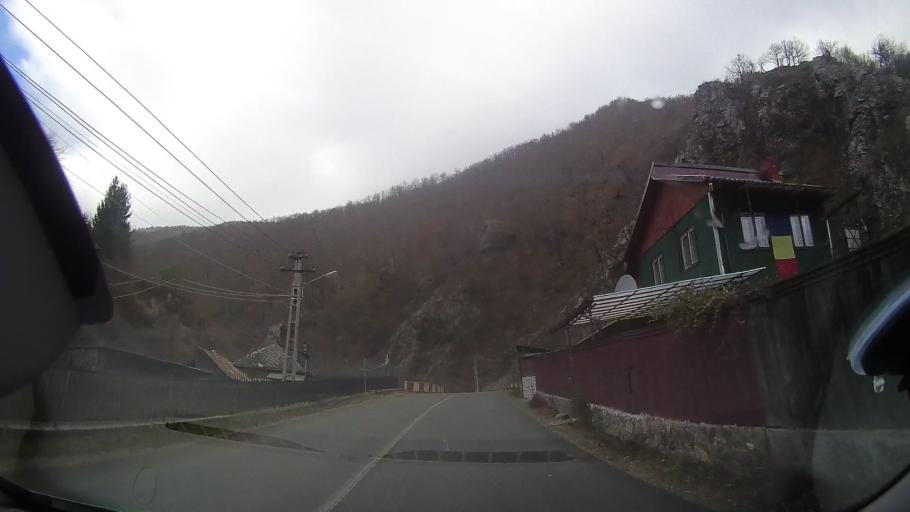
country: RO
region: Cluj
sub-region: Comuna Valea Ierii
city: Valea Ierii
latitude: 46.6856
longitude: 23.2778
